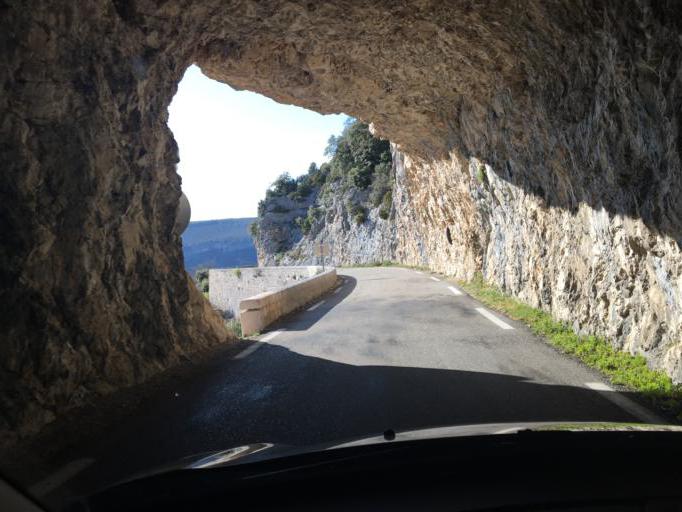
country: FR
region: Provence-Alpes-Cote d'Azur
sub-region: Departement du Vaucluse
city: Sault
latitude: 44.0567
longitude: 5.3269
